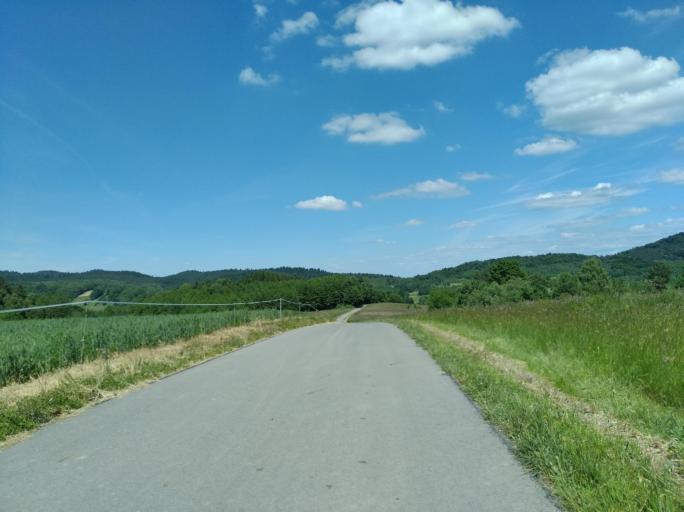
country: PL
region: Subcarpathian Voivodeship
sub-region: Powiat krosnienski
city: Wojaszowka
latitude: 49.7869
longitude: 21.7163
